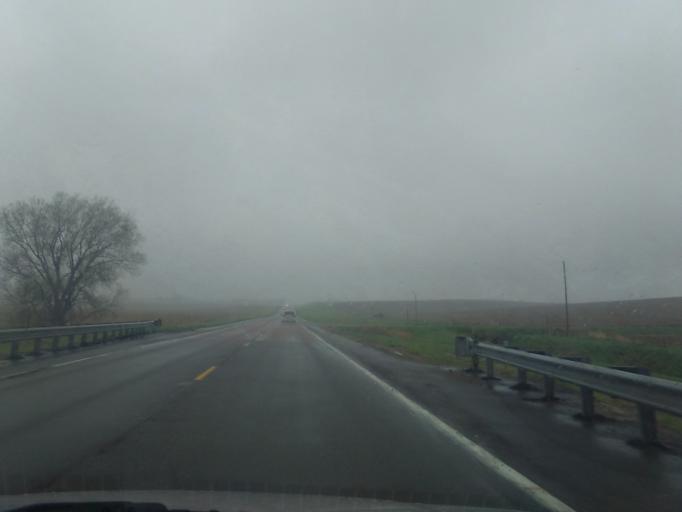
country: US
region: Nebraska
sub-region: Wayne County
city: Wayne
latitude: 42.2356
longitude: -97.1142
